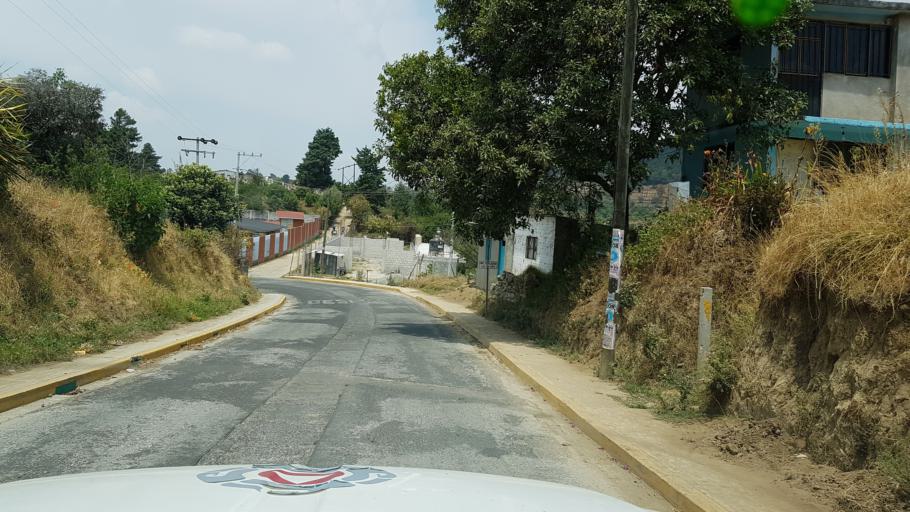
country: MX
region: Morelos
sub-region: Ocuituco
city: Huepalcalco (San Miguel)
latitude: 18.9163
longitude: -98.7434
